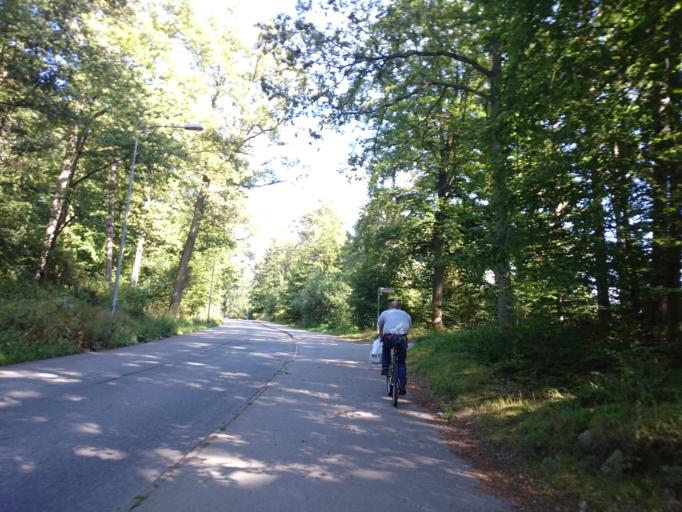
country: SE
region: Blekinge
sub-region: Karlshamns Kommun
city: Karlshamn
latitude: 56.1628
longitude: 14.8783
